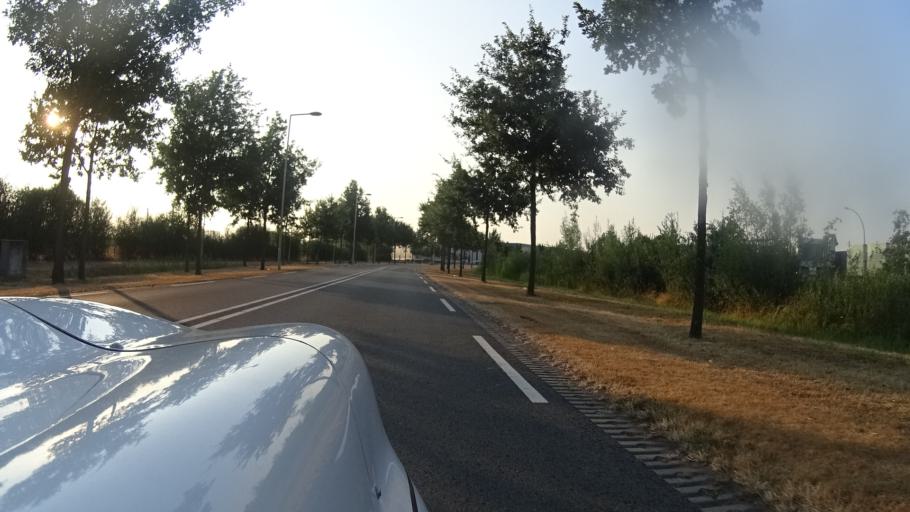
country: NL
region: Gelderland
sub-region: Gemeente Tiel
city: Tiel
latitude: 51.9134
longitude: 5.4482
